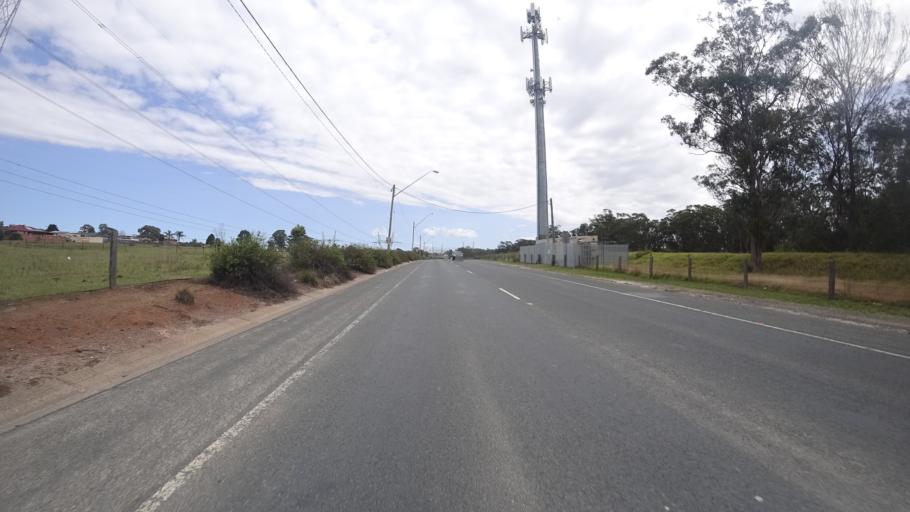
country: AU
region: New South Wales
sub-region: Campbelltown Municipality
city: Glenfield
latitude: -33.9683
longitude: 150.9051
